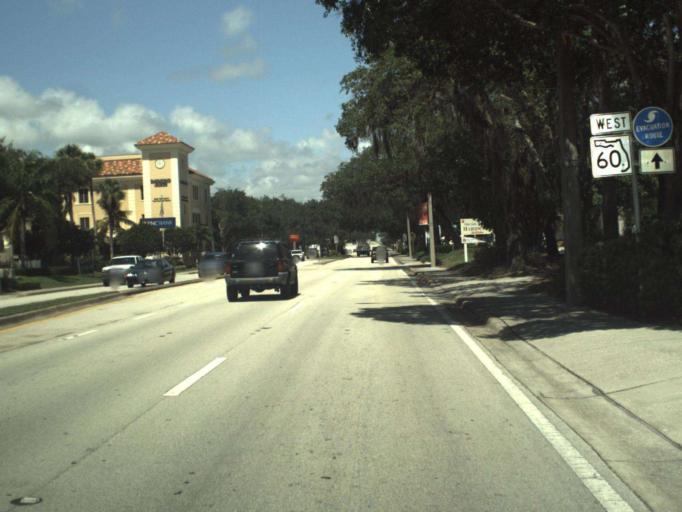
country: US
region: Florida
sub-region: Indian River County
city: Vero Beach
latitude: 27.6534
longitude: -80.3617
